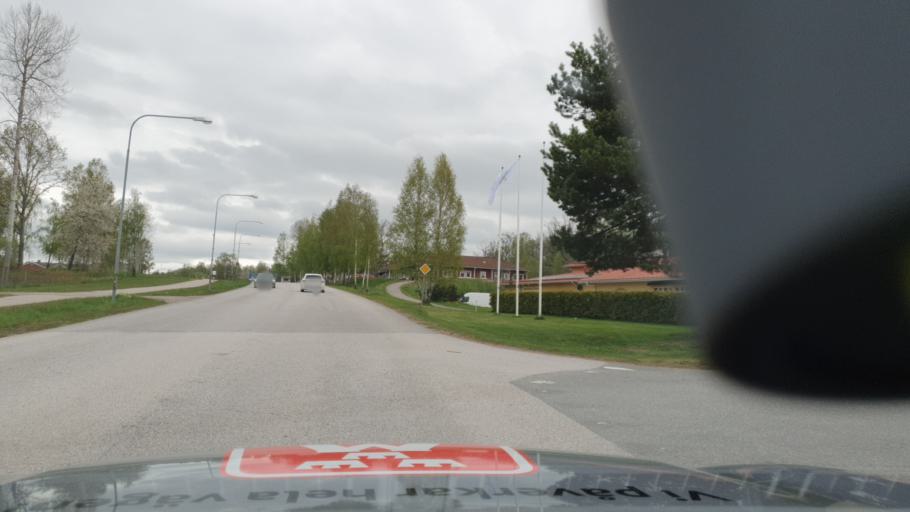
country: SE
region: Kalmar
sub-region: Vimmerby Kommun
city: Vimmerby
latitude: 57.6614
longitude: 15.8761
